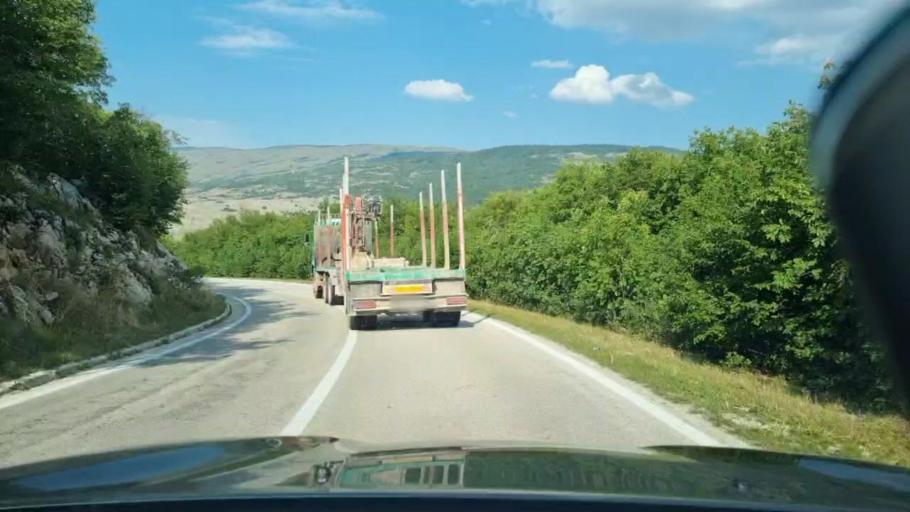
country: BA
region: Federation of Bosnia and Herzegovina
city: Glamoc
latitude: 43.9778
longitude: 16.9133
